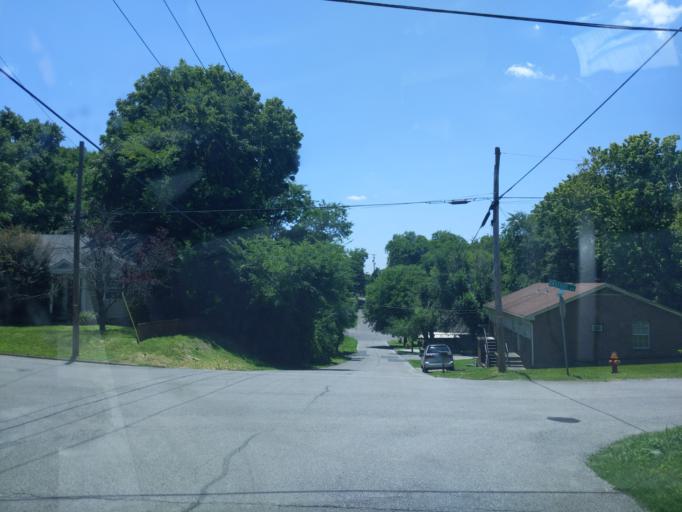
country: US
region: Tennessee
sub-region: Davidson County
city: Nashville
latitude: 36.1684
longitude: -86.7405
